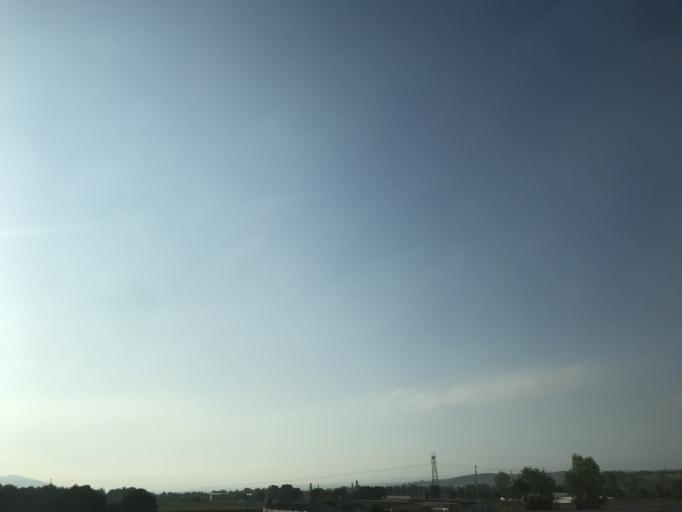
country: TR
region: Balikesir
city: Gobel
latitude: 40.0592
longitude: 28.2397
